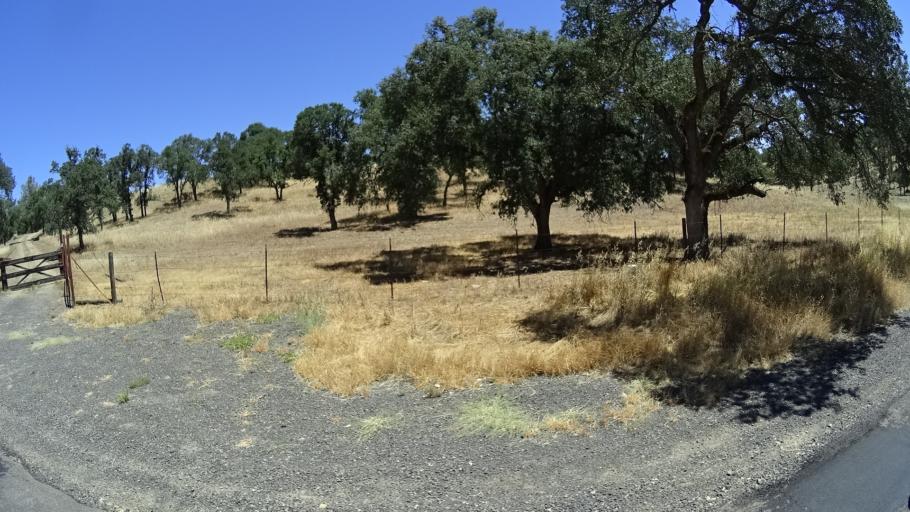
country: US
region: California
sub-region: Calaveras County
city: Copperopolis
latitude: 37.9836
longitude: -120.6828
